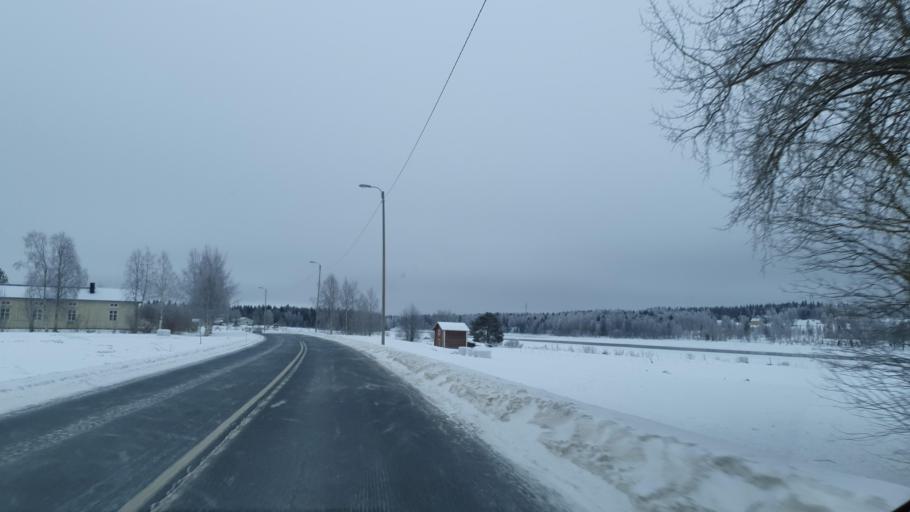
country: FI
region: Lapland
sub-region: Torniolaakso
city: Ylitornio
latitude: 66.1799
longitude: 23.8130
